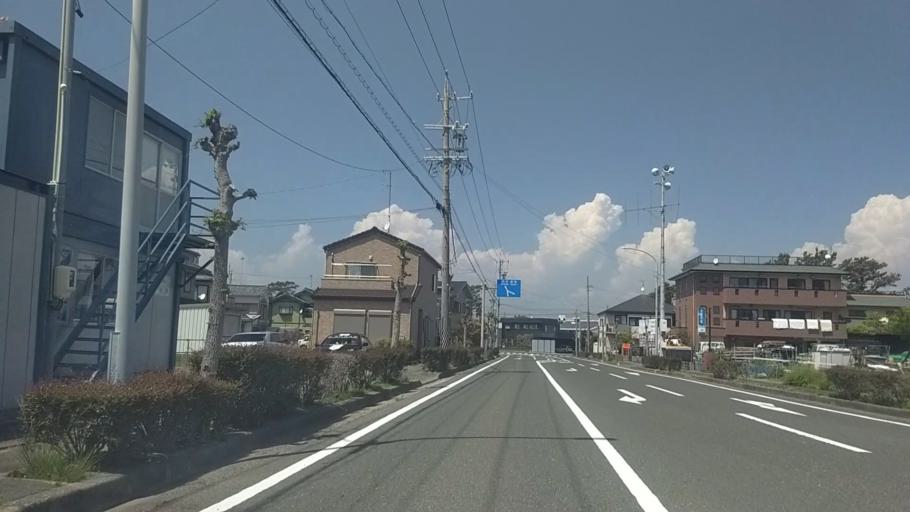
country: JP
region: Shizuoka
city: Kosai-shi
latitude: 34.6839
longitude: 137.5825
